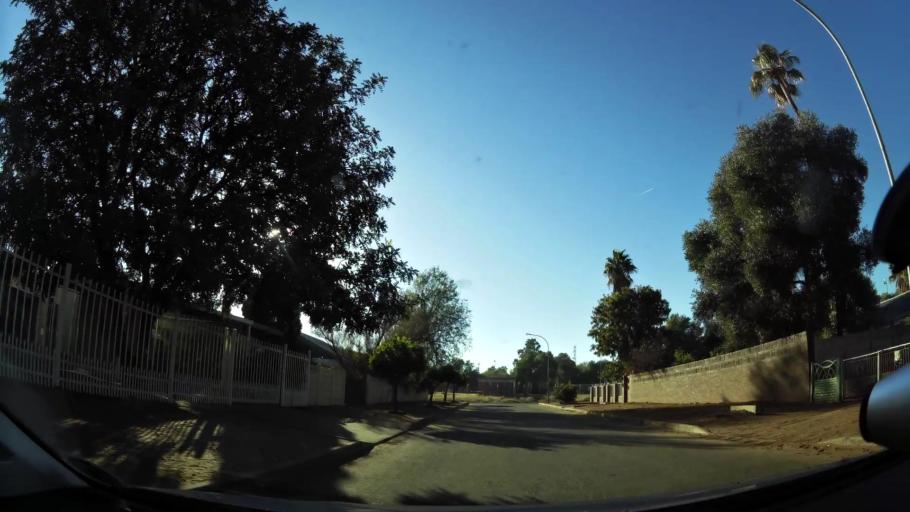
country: ZA
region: Northern Cape
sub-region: Frances Baard District Municipality
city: Kimberley
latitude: -28.7421
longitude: 24.7381
